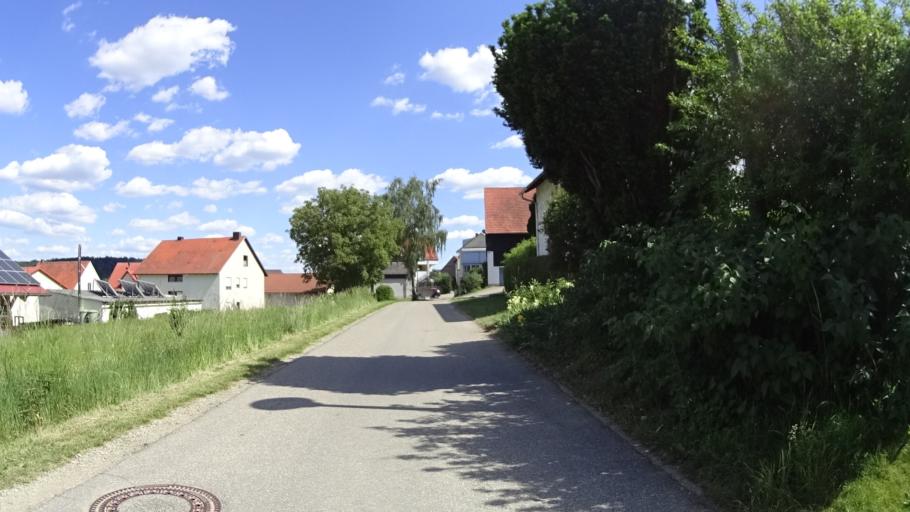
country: DE
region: Bavaria
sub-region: Regierungsbezirk Mittelfranken
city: Greding
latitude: 49.0615
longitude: 11.3191
